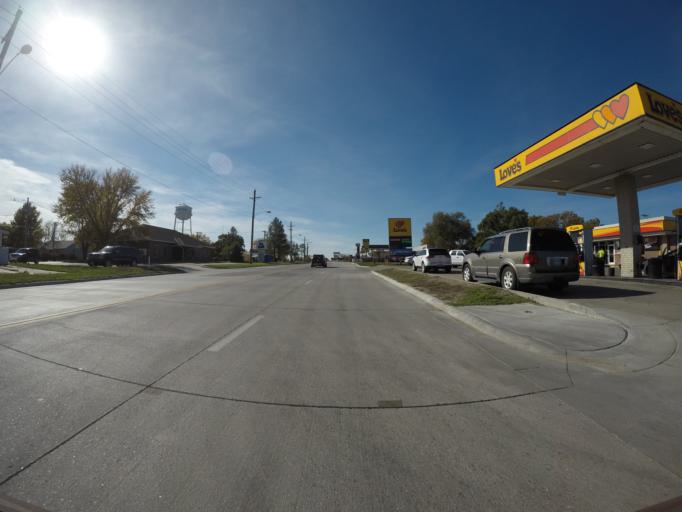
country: US
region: Kansas
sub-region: Norton County
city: Norton
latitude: 39.8386
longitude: -99.8924
